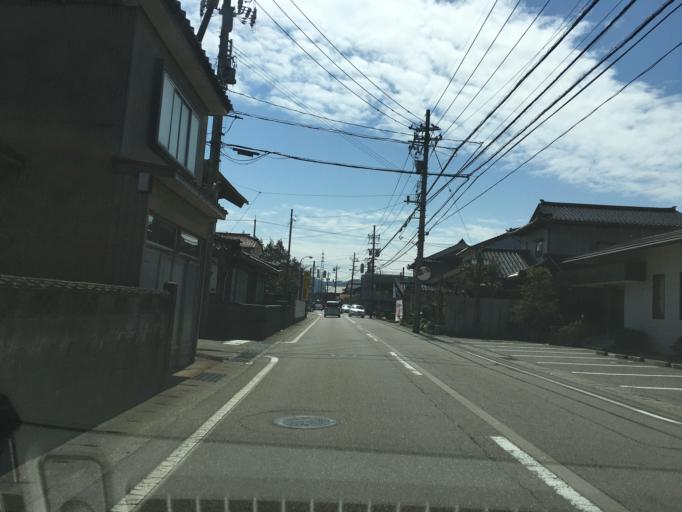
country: JP
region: Toyama
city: Himi
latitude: 36.8397
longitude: 136.9893
